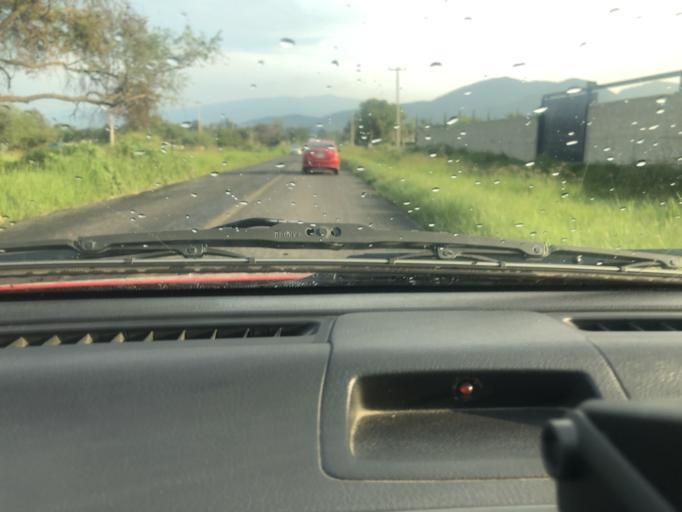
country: MX
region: Jalisco
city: Santa Cruz del Valle
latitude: 20.5479
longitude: -103.4206
